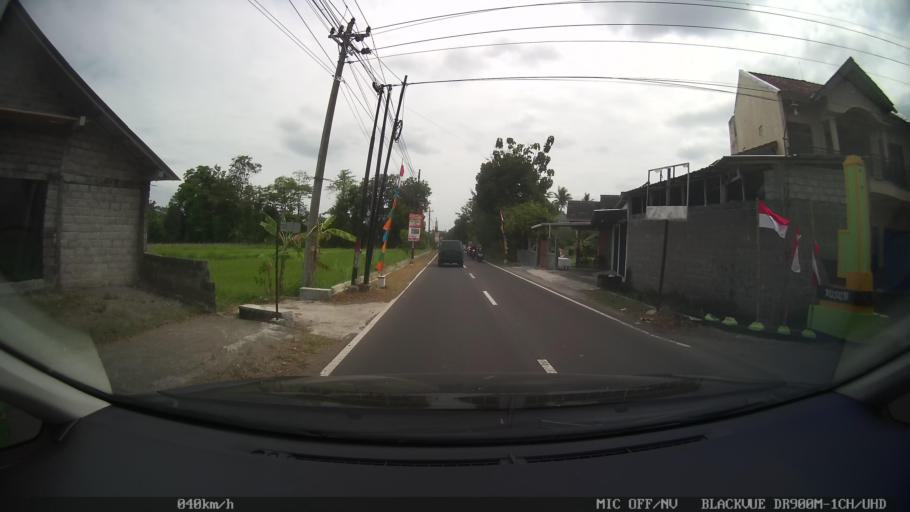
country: ID
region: Central Java
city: Candi Prambanan
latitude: -7.7291
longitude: 110.4650
